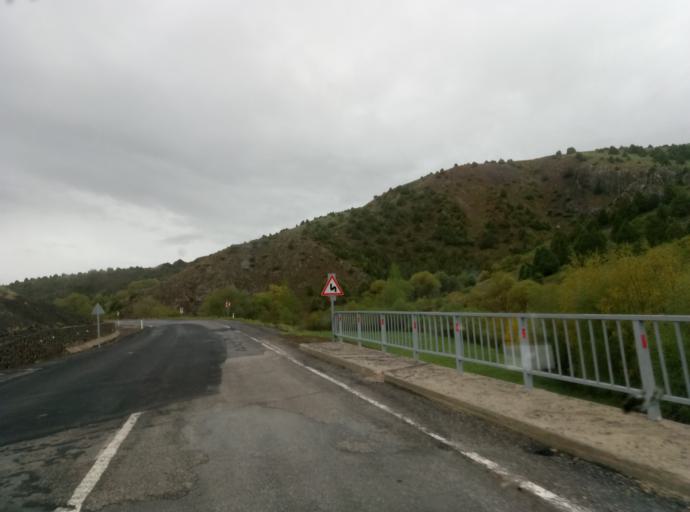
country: TR
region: Sivas
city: Zara
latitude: 39.9613
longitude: 37.7171
